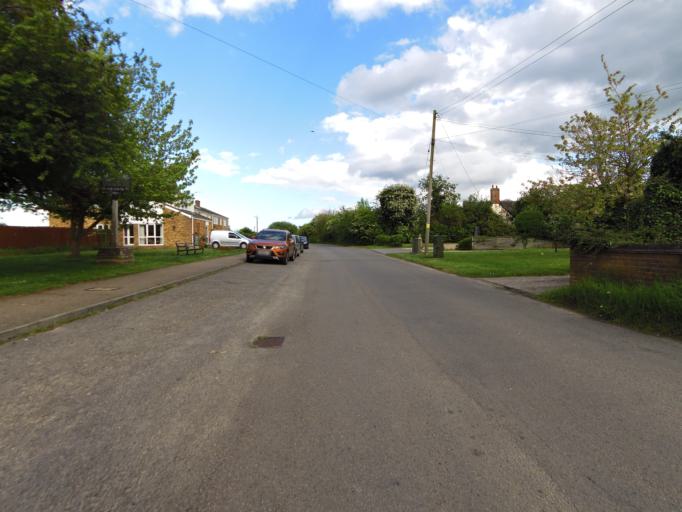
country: GB
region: England
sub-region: Suffolk
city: Stowmarket
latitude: 52.1966
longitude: 0.9600
